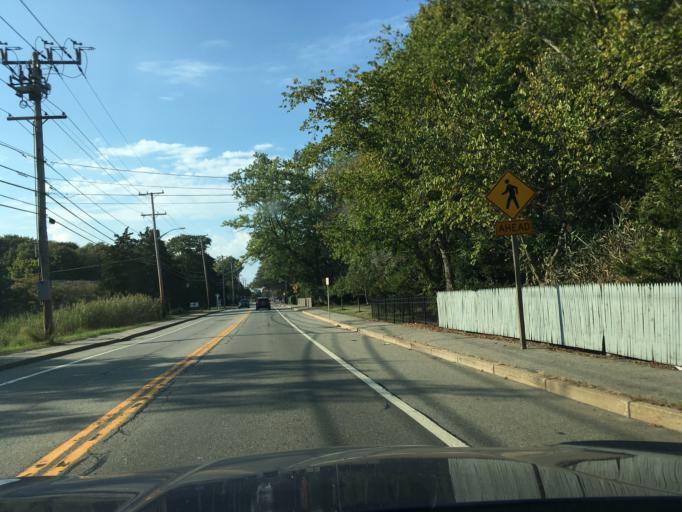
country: US
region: Rhode Island
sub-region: Bristol County
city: Barrington
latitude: 41.7444
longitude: -71.3146
